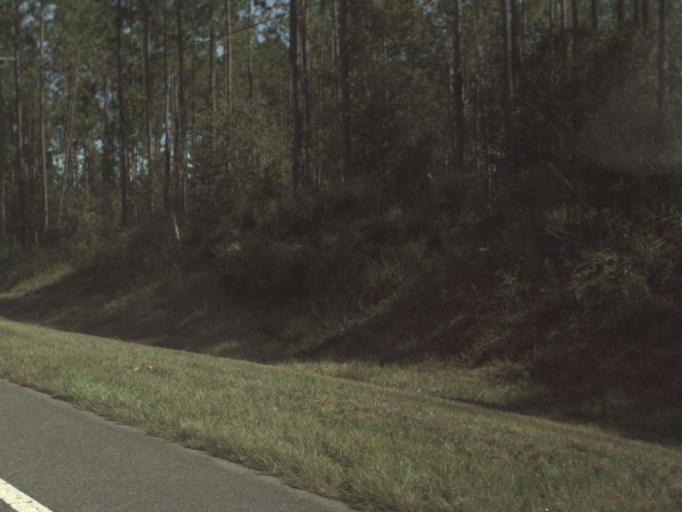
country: US
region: Florida
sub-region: Washington County
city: Chipley
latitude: 30.7139
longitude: -85.5572
